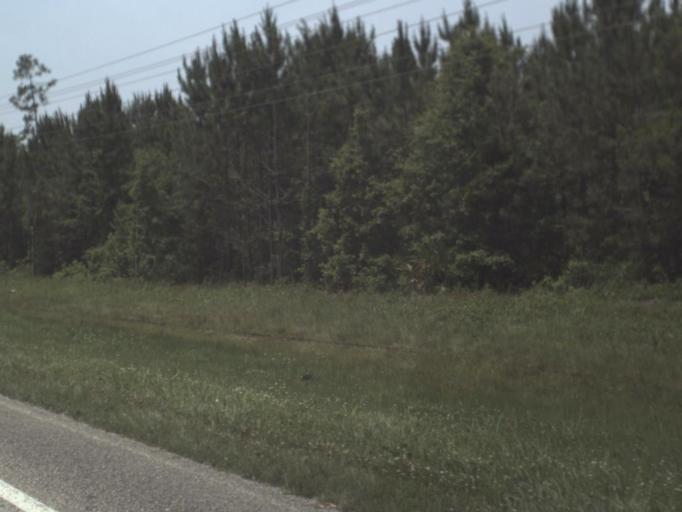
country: US
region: Florida
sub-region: Duval County
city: Baldwin
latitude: 30.1769
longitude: -82.0240
